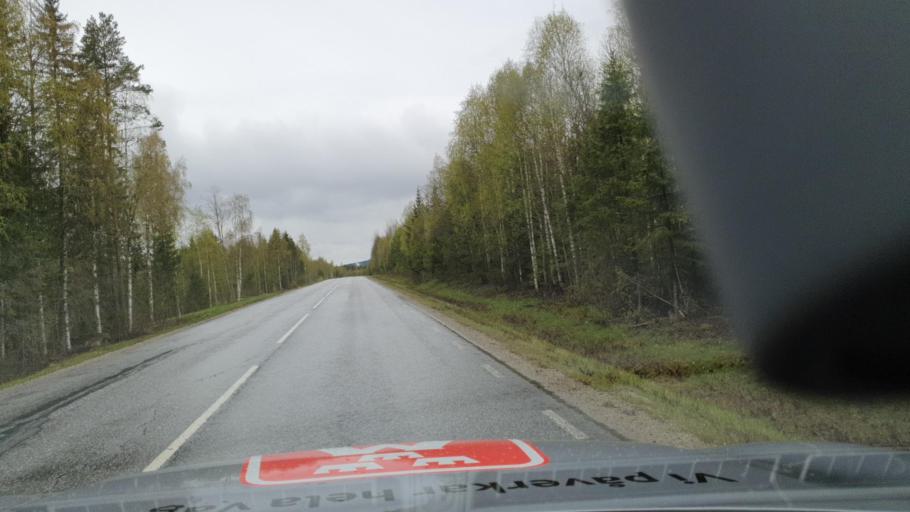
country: SE
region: Vaesternorrland
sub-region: OErnskoeldsviks Kommun
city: Bredbyn
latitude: 63.4846
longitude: 17.8807
